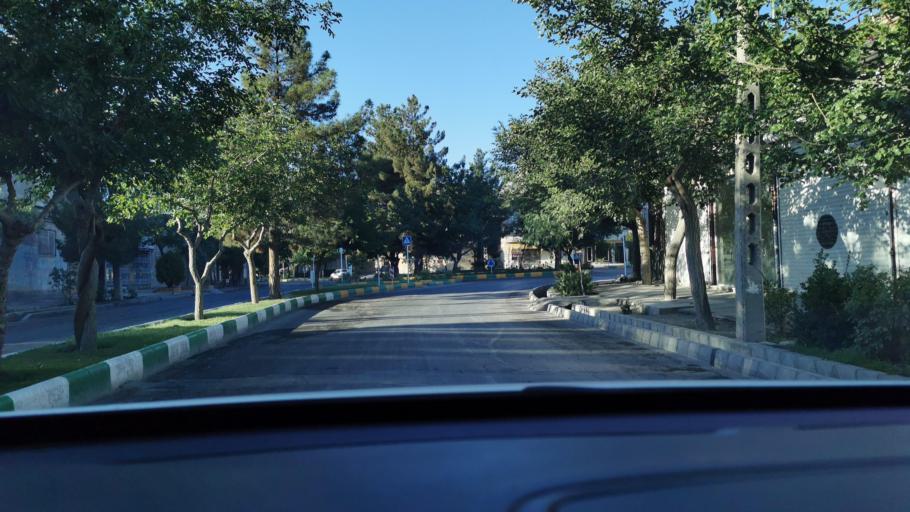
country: IR
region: Razavi Khorasan
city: Mashhad
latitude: 36.3606
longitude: 59.4904
